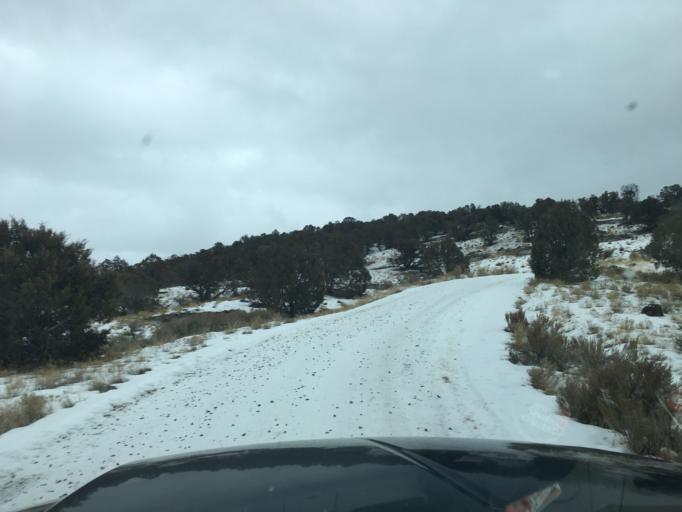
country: US
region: Colorado
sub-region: Garfield County
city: Parachute
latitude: 39.3480
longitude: -108.1700
